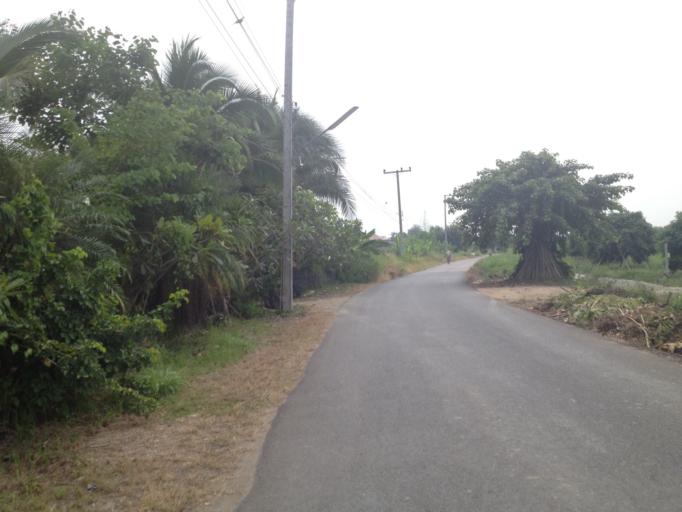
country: TH
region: Chiang Mai
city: Hang Dong
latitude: 18.6672
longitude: 98.8849
